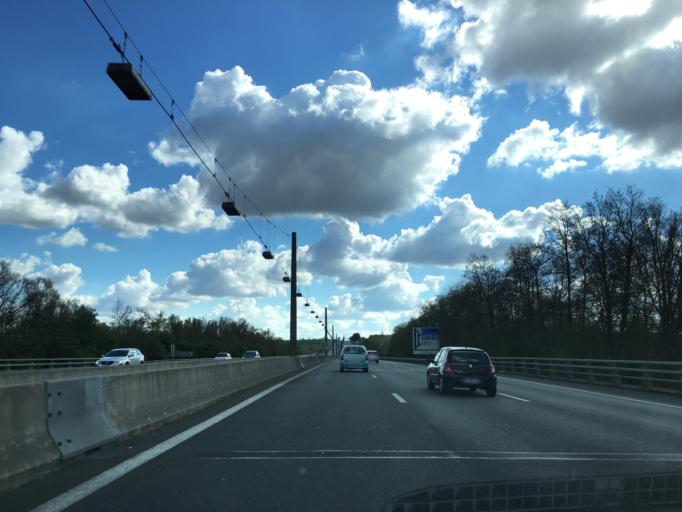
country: FR
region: Nord-Pas-de-Calais
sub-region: Departement du Pas-de-Calais
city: Fampoux
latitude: 50.2957
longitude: 2.8849
